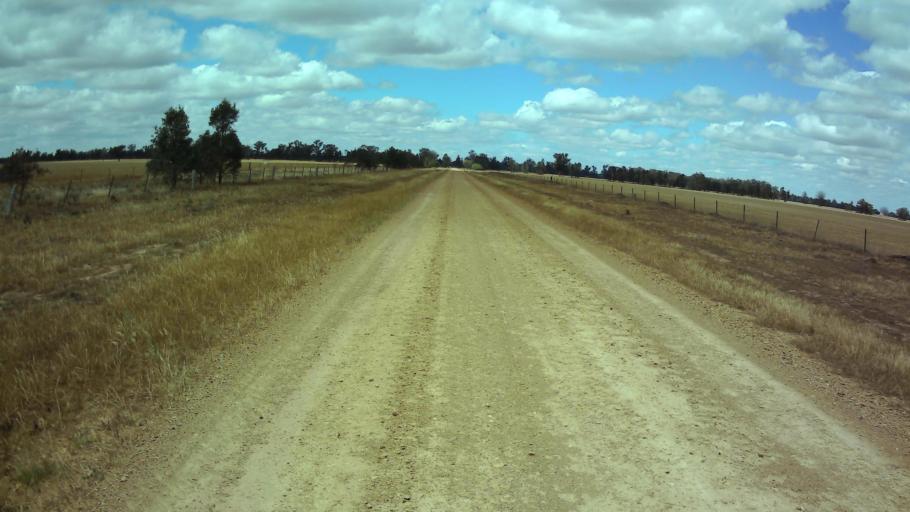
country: AU
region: New South Wales
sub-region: Weddin
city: Grenfell
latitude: -34.0081
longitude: 147.9169
